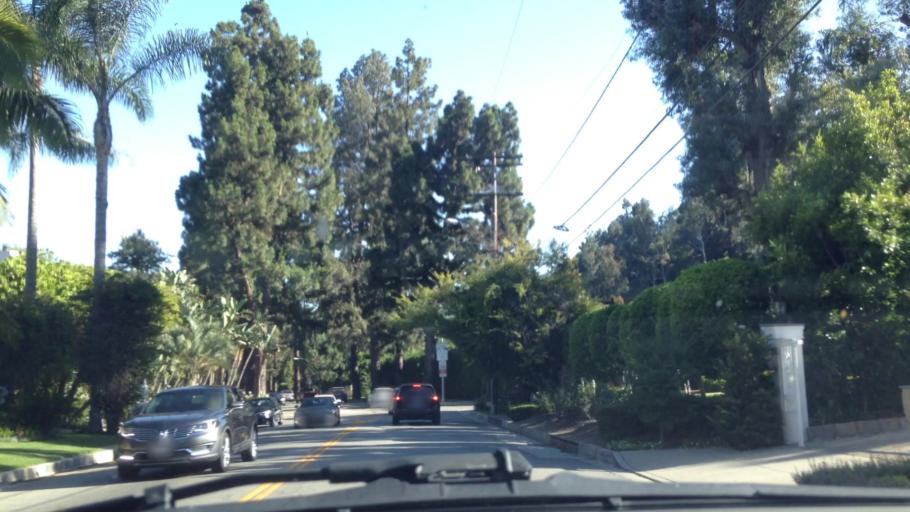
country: US
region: California
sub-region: Los Angeles County
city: Beverly Hills
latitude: 34.1021
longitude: -118.4061
